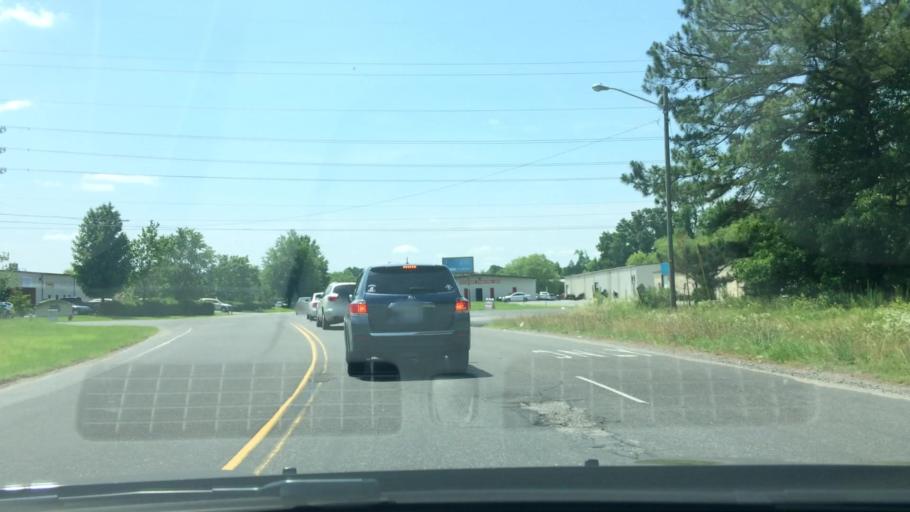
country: US
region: North Carolina
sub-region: Pitt County
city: Windsor
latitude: 35.5636
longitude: -77.3558
